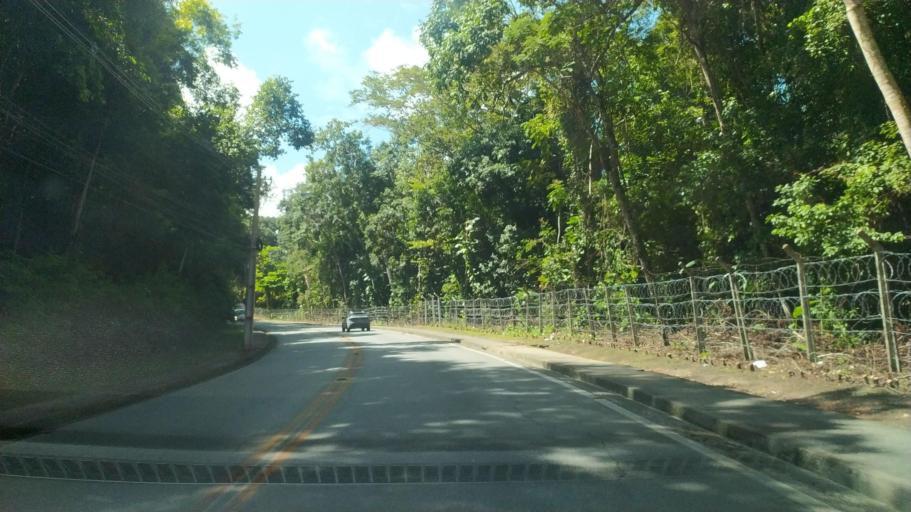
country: BR
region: Alagoas
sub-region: Maceio
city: Maceio
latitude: -9.5971
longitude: -35.7377
